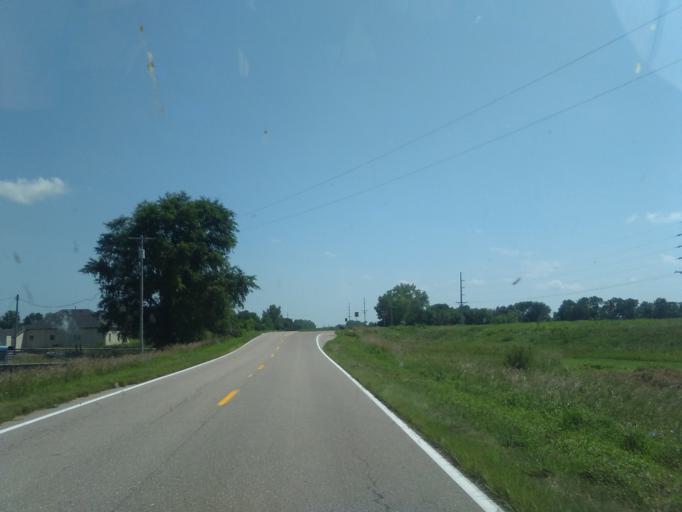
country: US
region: Nebraska
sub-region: Phelps County
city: Holdrege
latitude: 40.7118
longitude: -99.3793
